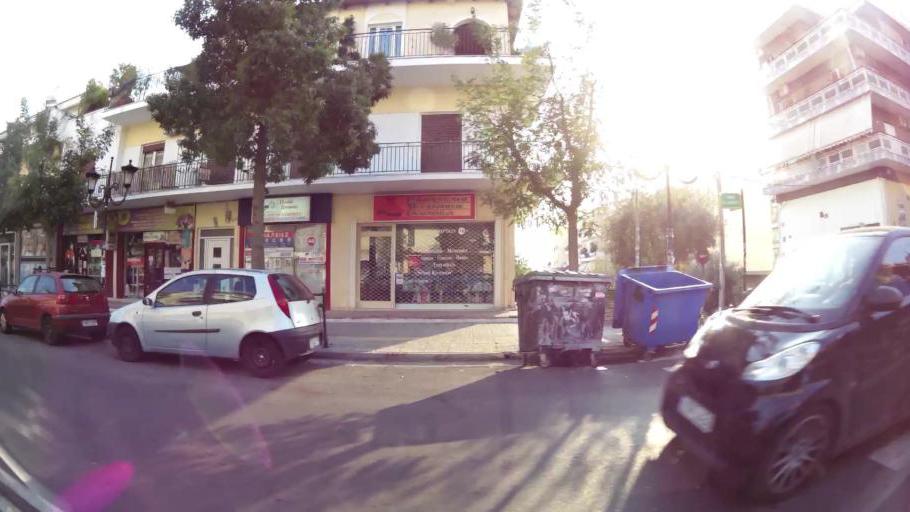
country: GR
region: Attica
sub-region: Nomarchia Athinas
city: Petroupolis
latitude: 38.0438
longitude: 23.6807
